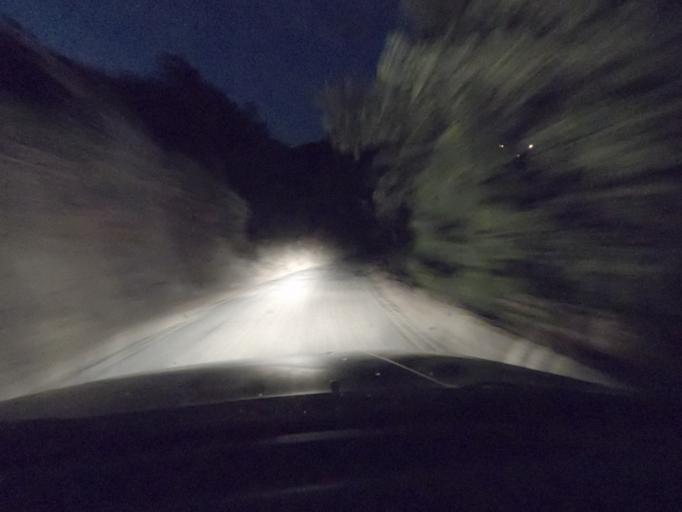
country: PT
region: Vila Real
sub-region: Santa Marta de Penaguiao
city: Santa Marta de Penaguiao
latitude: 41.2046
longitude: -7.8457
